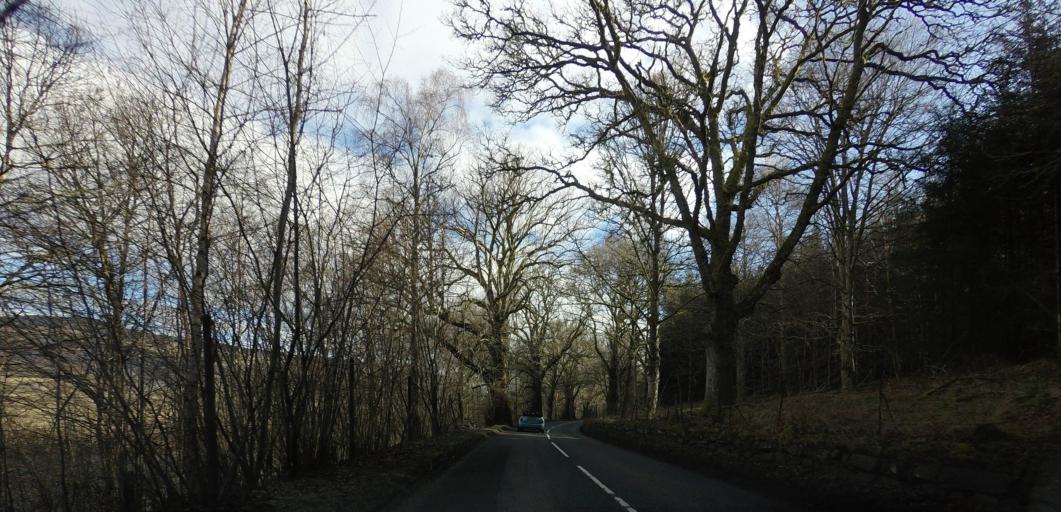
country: GB
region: Scotland
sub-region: Perth and Kinross
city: Aberfeldy
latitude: 56.6074
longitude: -3.9422
